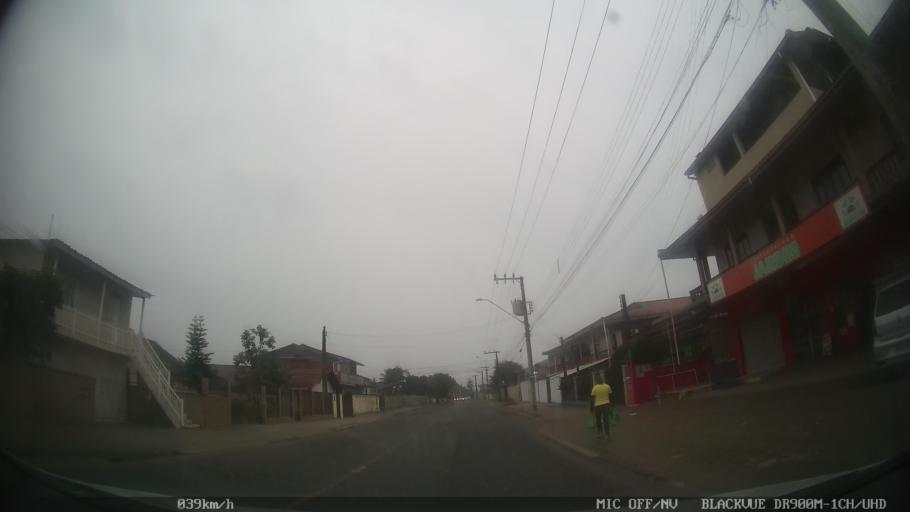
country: BR
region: Santa Catarina
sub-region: Joinville
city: Joinville
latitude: -26.2710
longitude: -48.7993
